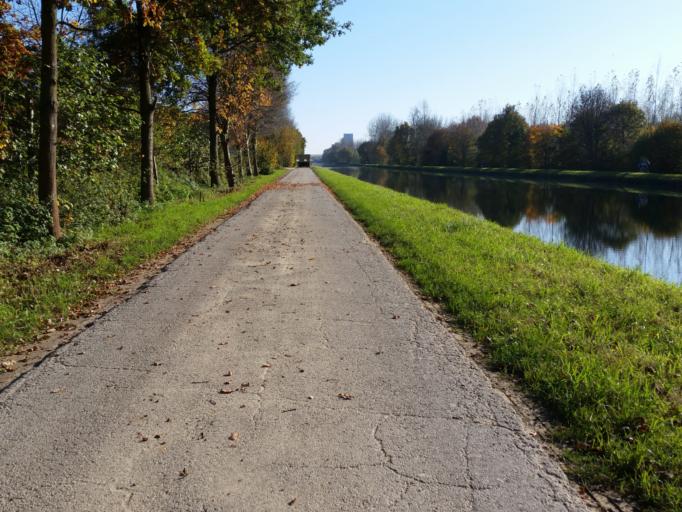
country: BE
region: Flanders
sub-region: Provincie Vlaams-Brabant
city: Herent
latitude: 50.9384
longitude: 4.6678
